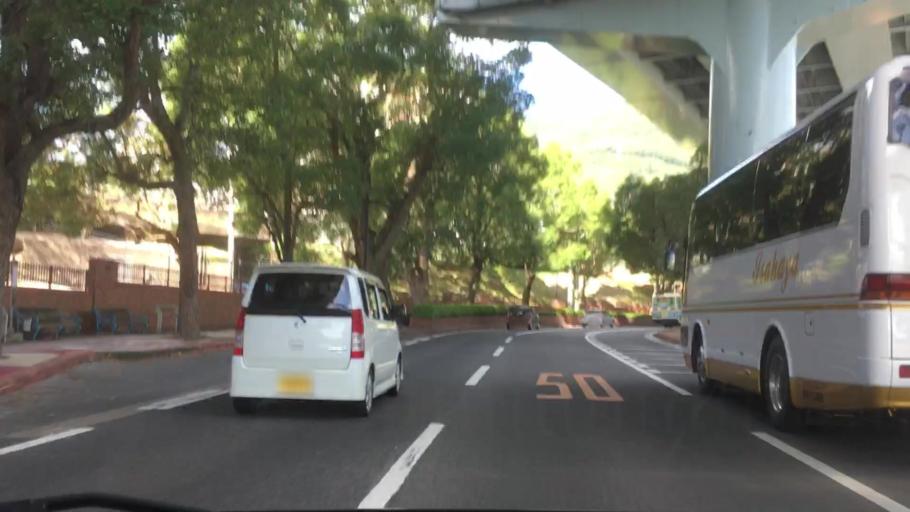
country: JP
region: Nagasaki
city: Sasebo
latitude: 33.1711
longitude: 129.7137
